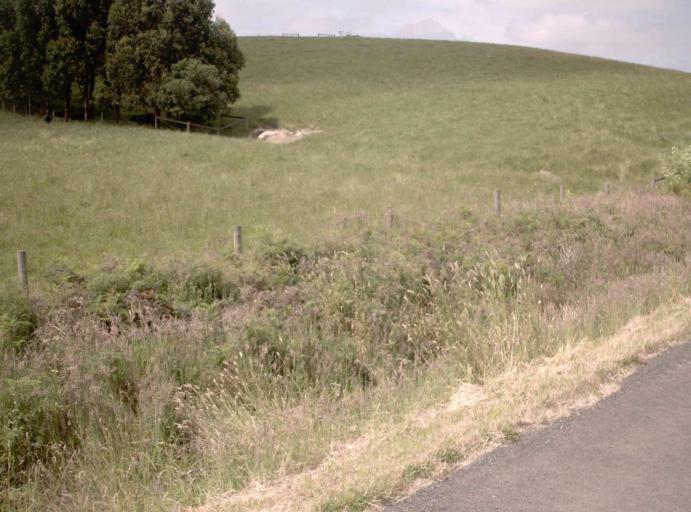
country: AU
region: Victoria
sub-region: Baw Baw
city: Warragul
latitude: -38.4116
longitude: 146.0476
